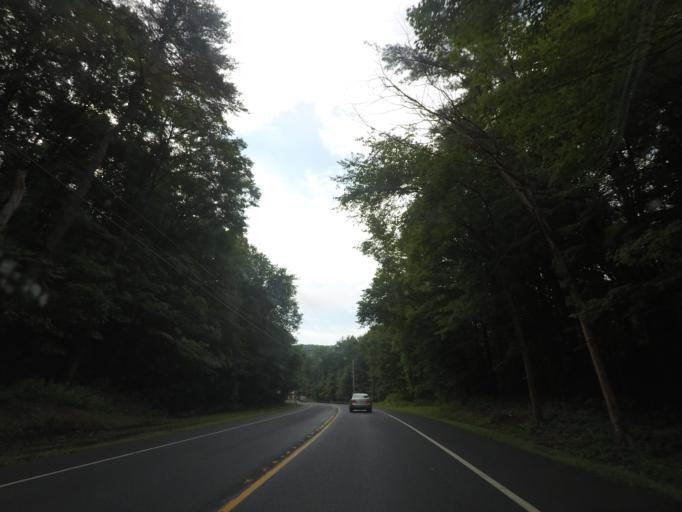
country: US
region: New York
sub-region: Rensselaer County
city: Nassau
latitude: 42.4961
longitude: -73.5530
